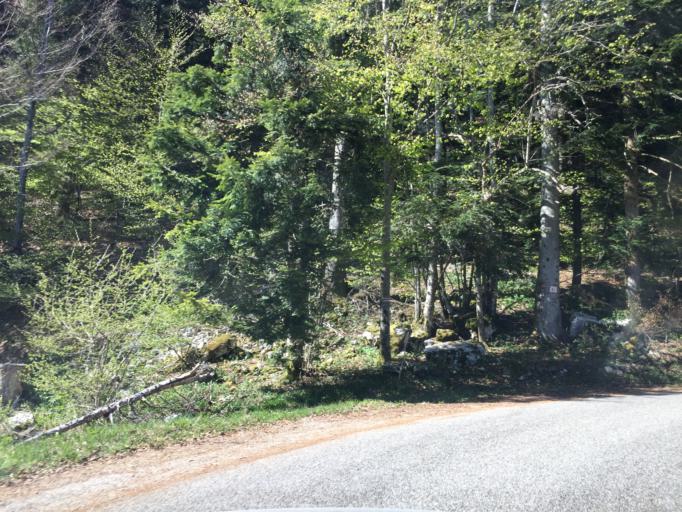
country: FR
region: Rhone-Alpes
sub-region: Departement de la Savoie
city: Novalaise
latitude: 45.5913
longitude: 5.8155
